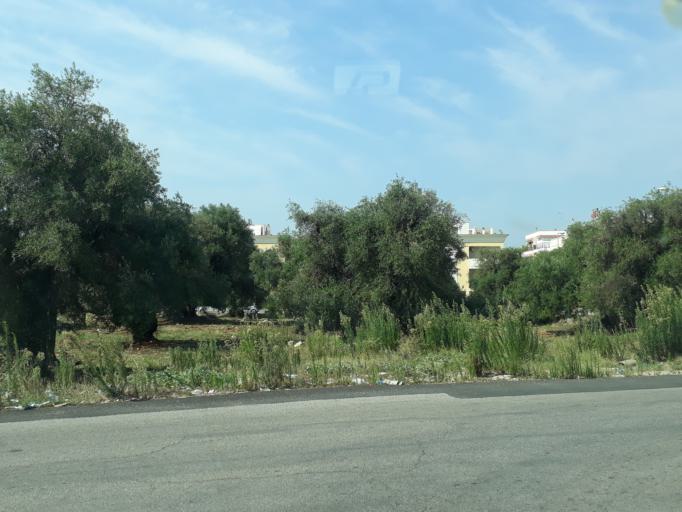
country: IT
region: Apulia
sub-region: Provincia di Brindisi
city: Carovigno
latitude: 40.6998
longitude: 17.6668
